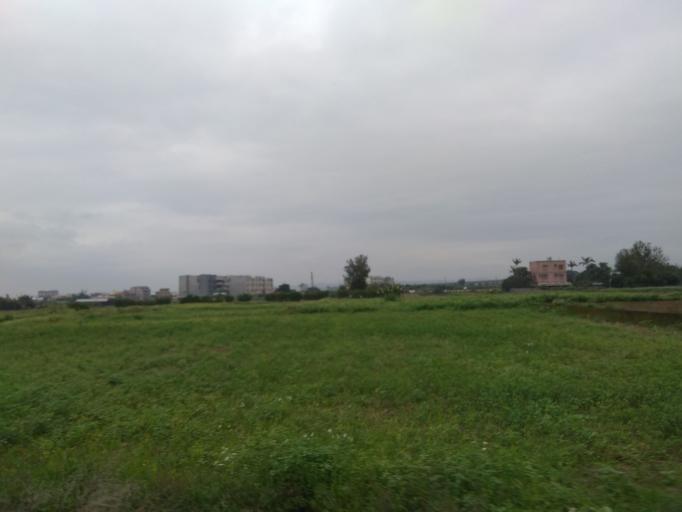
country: TW
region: Taiwan
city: Taoyuan City
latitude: 25.0307
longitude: 121.2237
